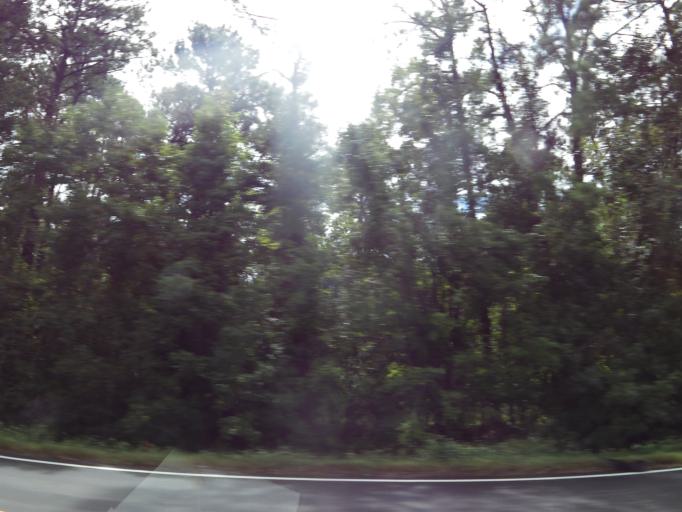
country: US
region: Florida
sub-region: Duval County
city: Baldwin
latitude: 30.1468
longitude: -82.0132
